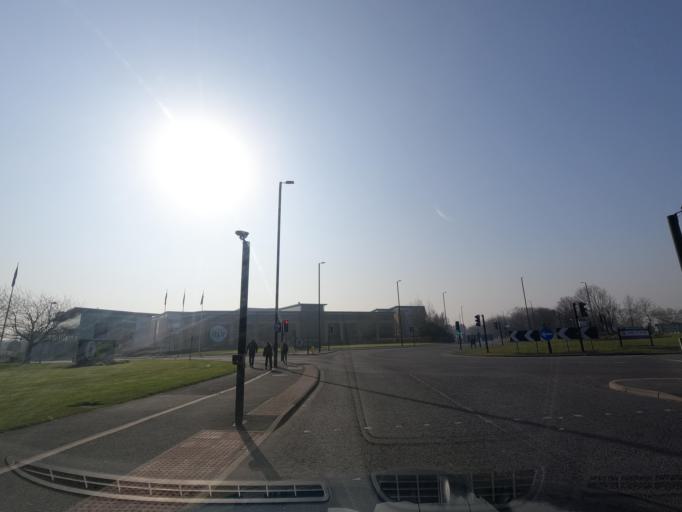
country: GB
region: England
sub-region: Newcastle upon Tyne
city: Gosforth
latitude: 55.0202
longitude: -1.5845
